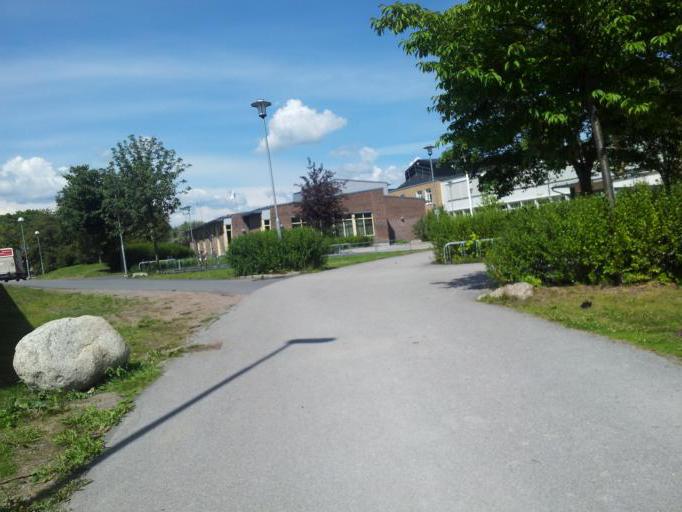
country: SE
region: Uppsala
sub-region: Uppsala Kommun
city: Uppsala
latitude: 59.8631
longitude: 17.6656
